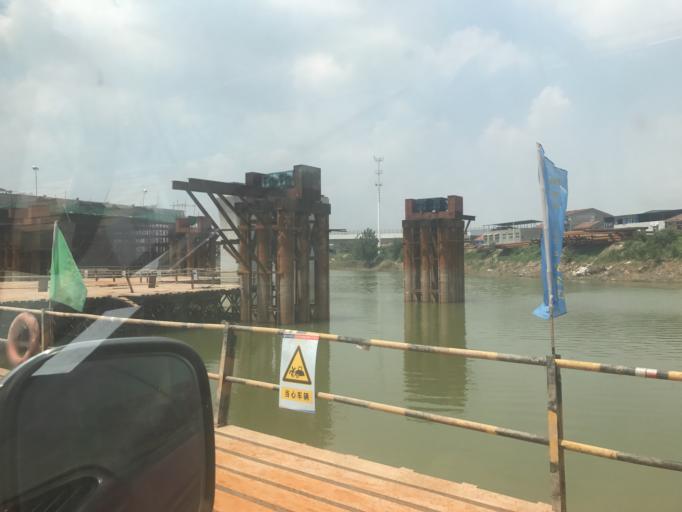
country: CN
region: Hubei
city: Zhanjiaji
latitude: 30.6856
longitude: 114.3396
